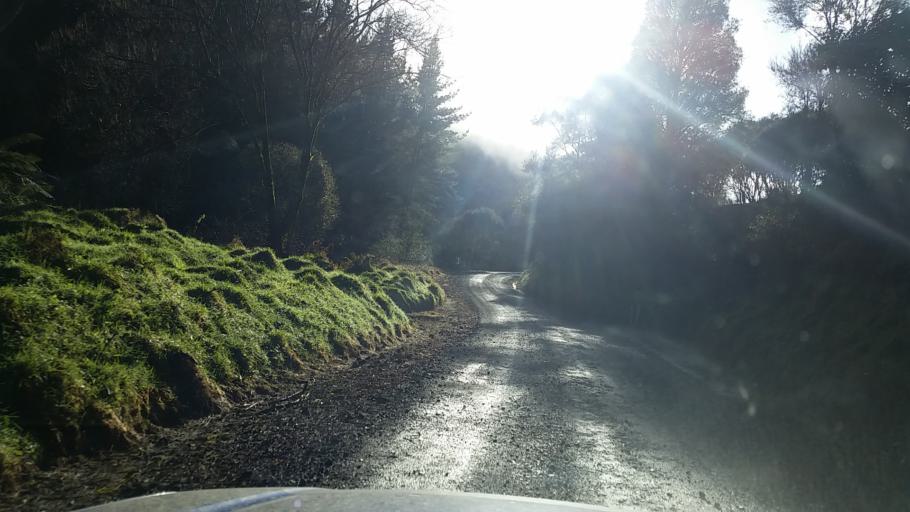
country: NZ
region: Taranaki
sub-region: South Taranaki District
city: Eltham
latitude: -39.3258
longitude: 174.6497
